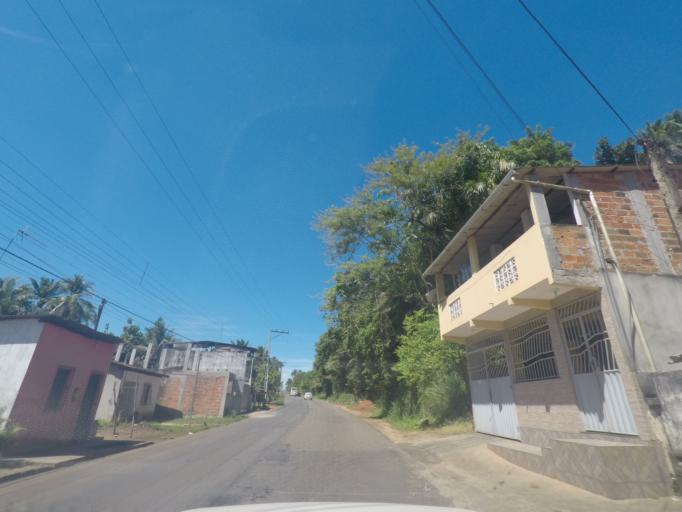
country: BR
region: Bahia
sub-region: Valenca
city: Valenca
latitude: -13.4371
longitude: -39.0790
